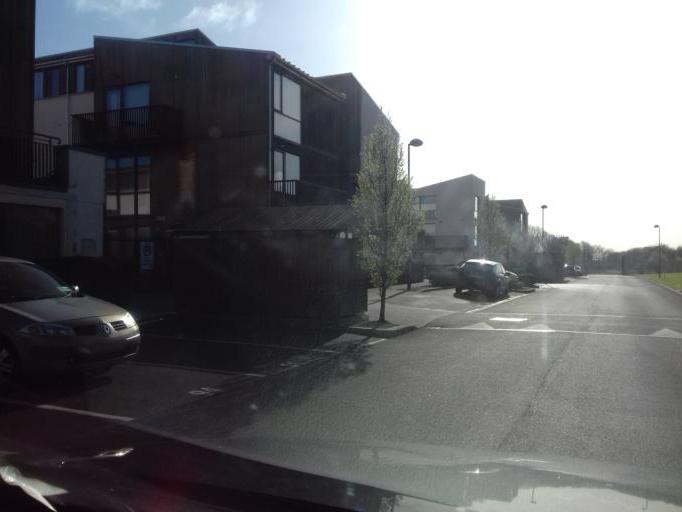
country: IE
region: Leinster
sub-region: Dublin City
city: Finglas
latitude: 53.3979
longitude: -6.2888
